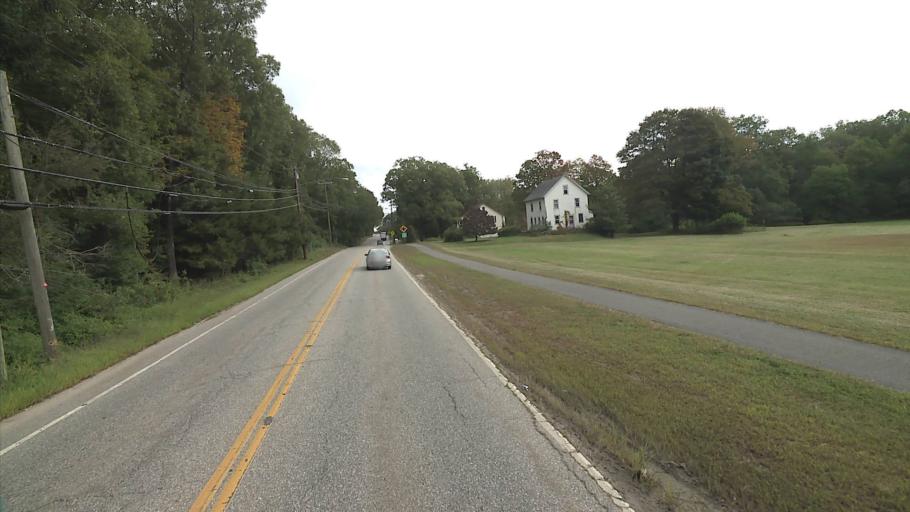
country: US
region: Connecticut
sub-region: Tolland County
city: Storrs
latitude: 41.7957
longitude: -72.2503
